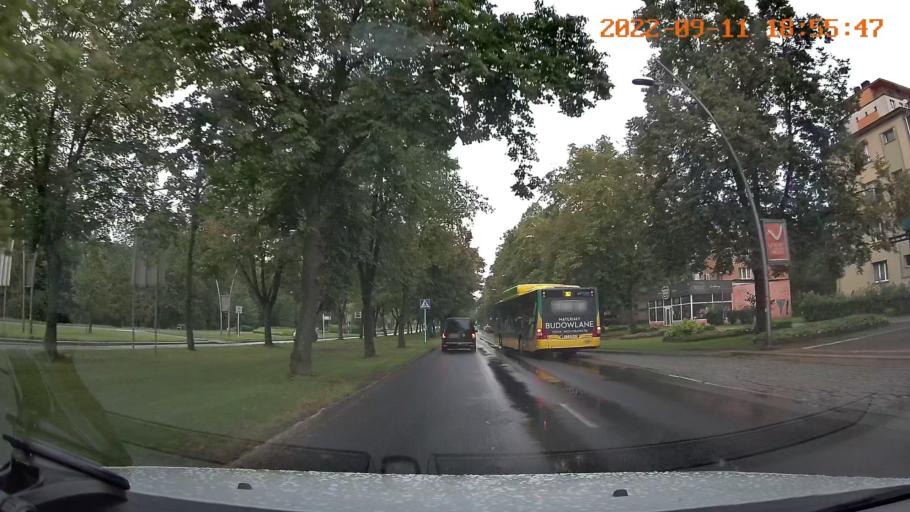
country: PL
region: Silesian Voivodeship
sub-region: Tychy
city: Tychy
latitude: 50.1158
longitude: 18.9926
